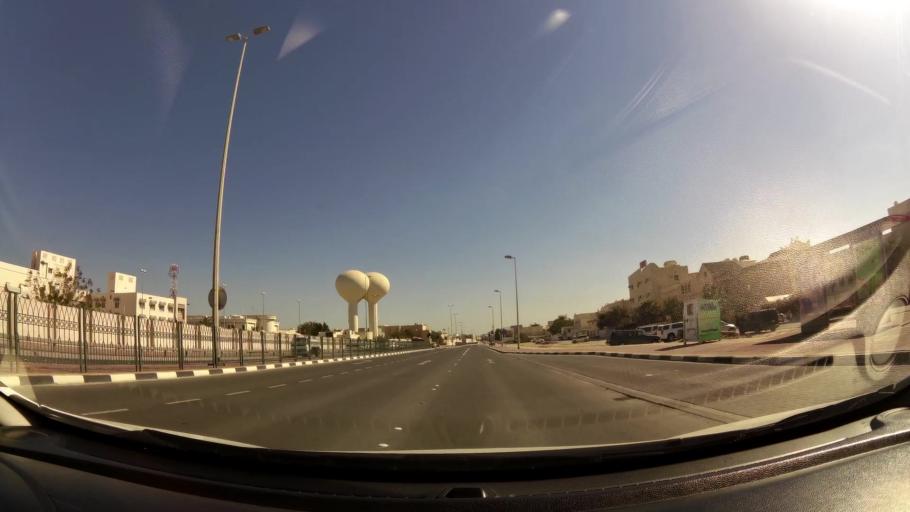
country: BH
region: Muharraq
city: Al Hadd
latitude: 26.2507
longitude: 50.6513
